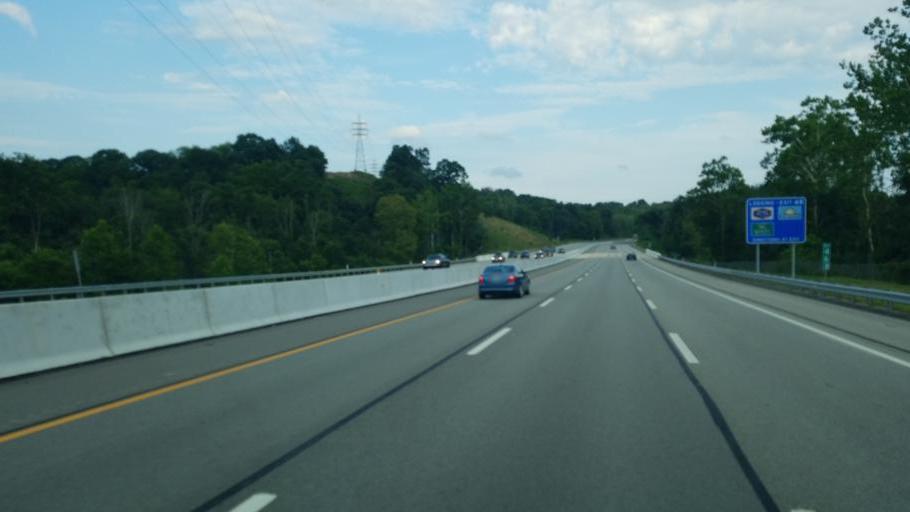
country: US
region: Pennsylvania
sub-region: Allegheny County
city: Oakmont
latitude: 40.5523
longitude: -79.8320
